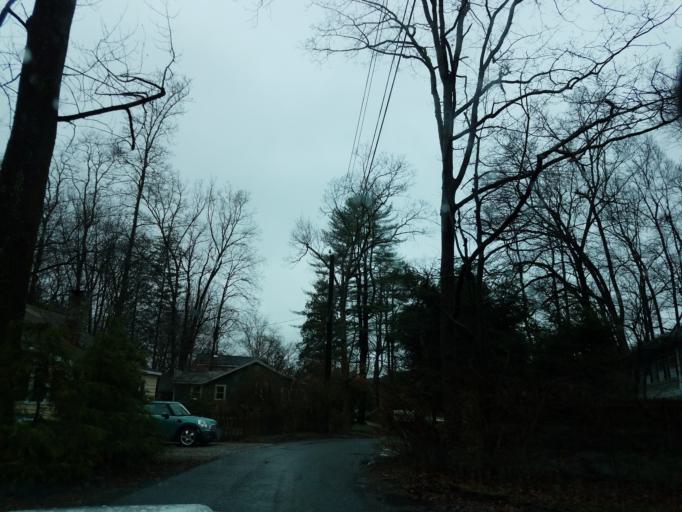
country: US
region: Connecticut
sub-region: Fairfield County
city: Ridgefield
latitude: 41.3413
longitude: -73.4911
